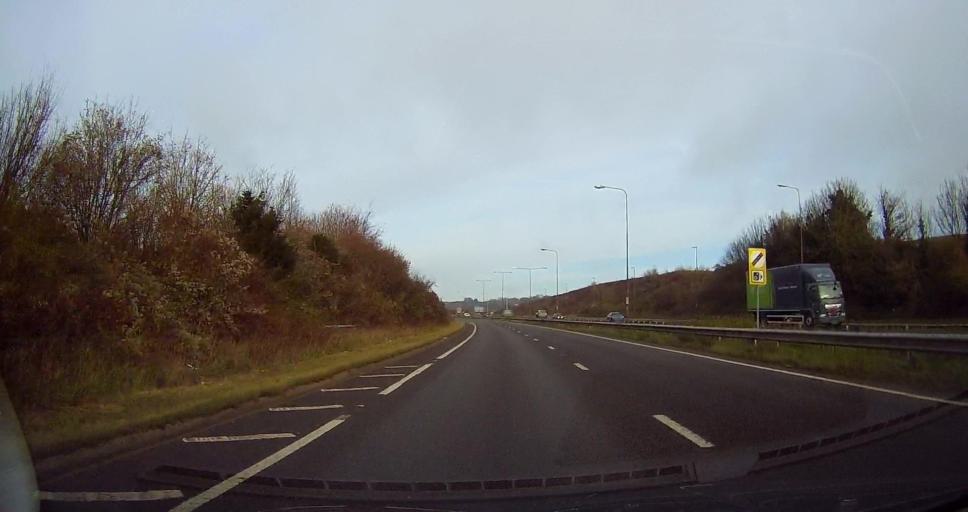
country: GB
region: England
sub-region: West Sussex
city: Hassocks
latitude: 50.8912
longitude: -0.1629
